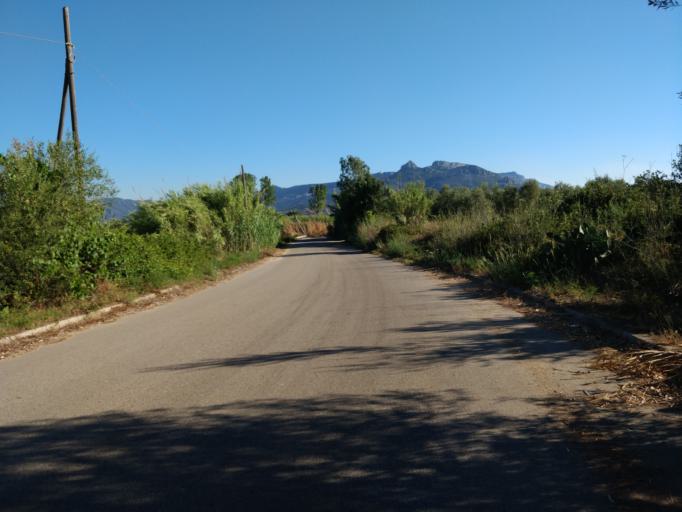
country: IT
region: Sardinia
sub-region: Provincia di Ogliastra
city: Girasole
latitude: 39.9531
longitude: 9.6716
